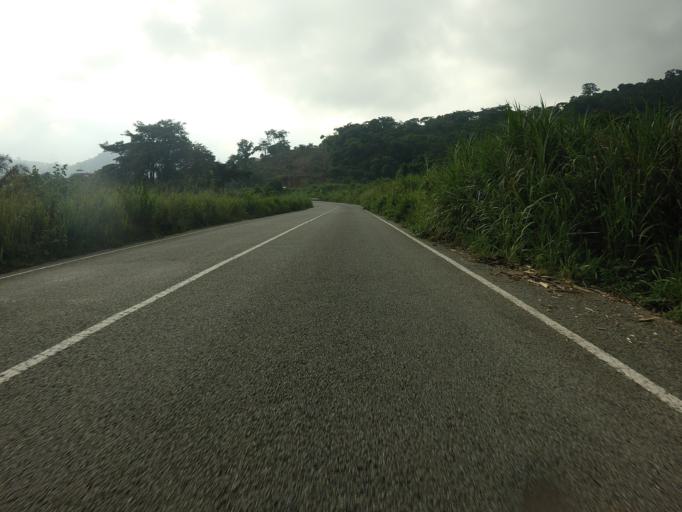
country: GH
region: Volta
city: Ho
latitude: 6.8105
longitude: 0.4238
